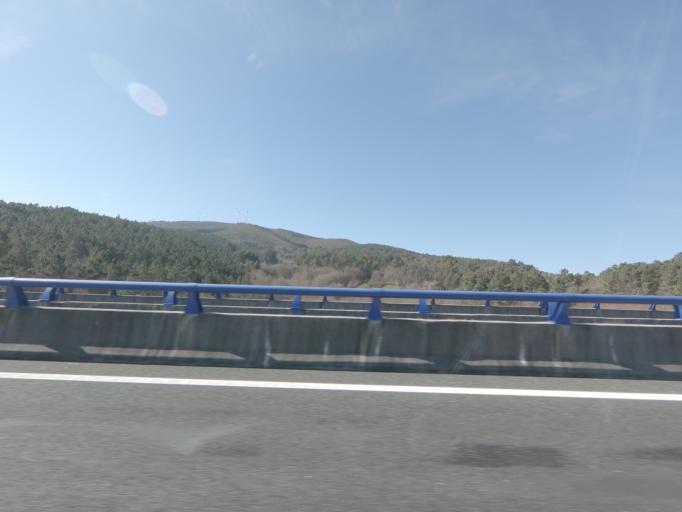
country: ES
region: Galicia
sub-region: Provincia de Ourense
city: Pinor
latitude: 42.5135
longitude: -8.0205
